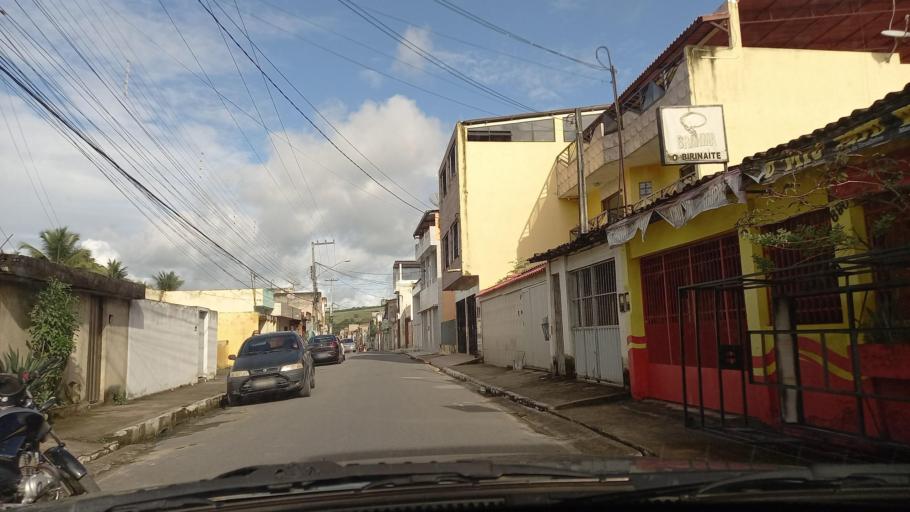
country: BR
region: Pernambuco
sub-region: Palmares
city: Palmares
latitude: -8.6820
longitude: -35.5945
